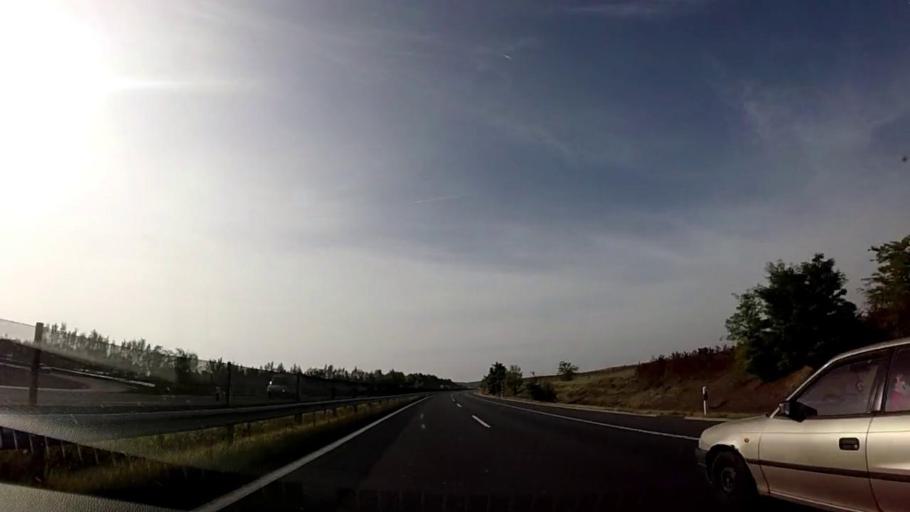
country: HU
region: Somogy
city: Zamardi
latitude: 46.8568
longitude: 17.9629
